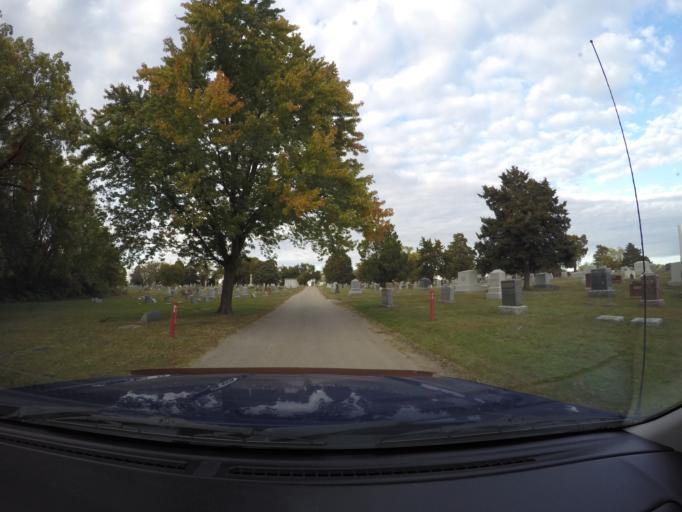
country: US
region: Kansas
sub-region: Shawnee County
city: Topeka
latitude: 39.0392
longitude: -95.6530
